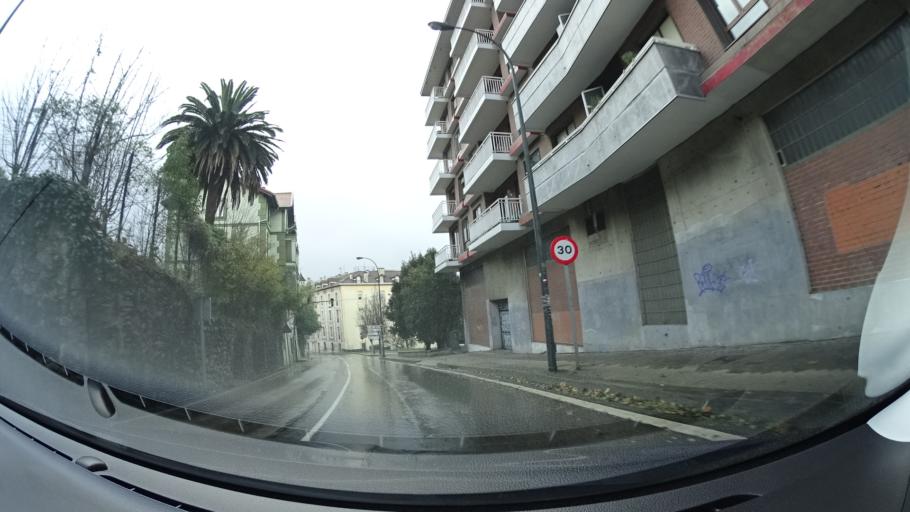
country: ES
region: Basque Country
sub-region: Bizkaia
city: Santutxu
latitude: 43.2600
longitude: -2.9121
